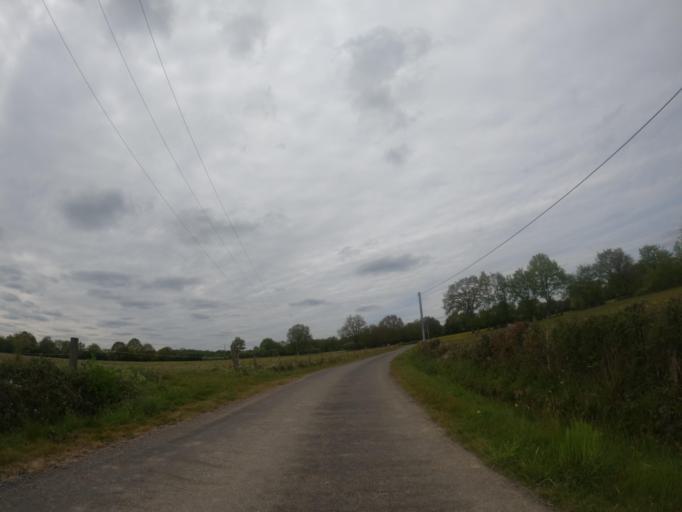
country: FR
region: Pays de la Loire
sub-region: Departement de la Loire-Atlantique
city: Saint-Aubin-des-Chateaux
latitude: 47.7299
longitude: -1.4510
